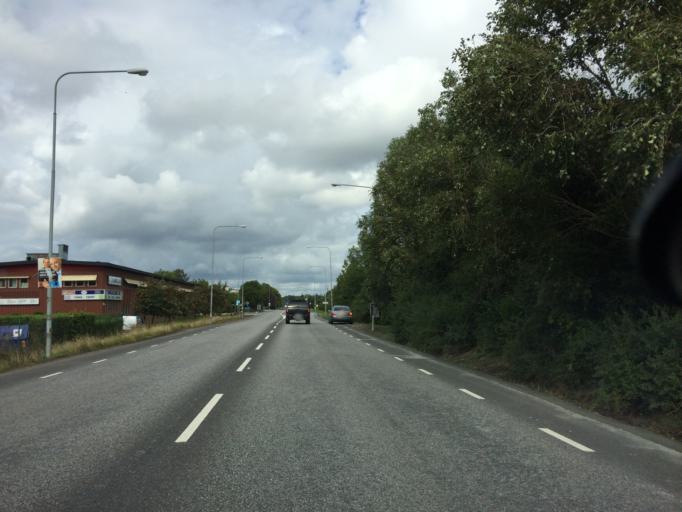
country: SE
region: Stockholm
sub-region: Sollentuna Kommun
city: Sollentuna
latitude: 59.4557
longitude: 17.9243
